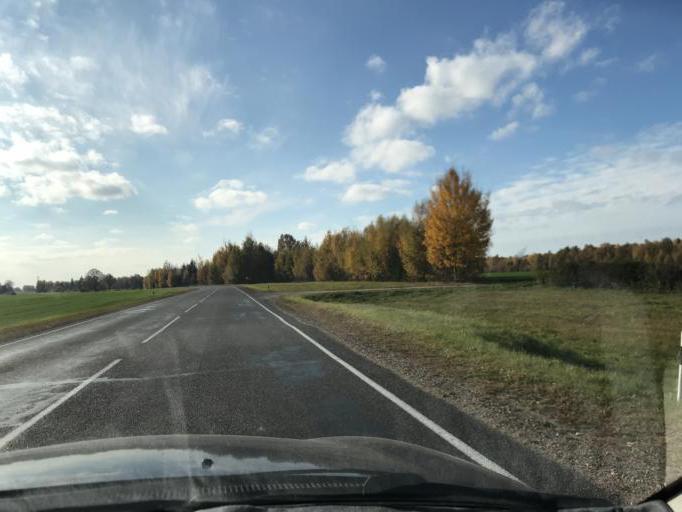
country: BY
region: Grodnenskaya
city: Voranava
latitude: 54.1851
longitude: 25.3379
